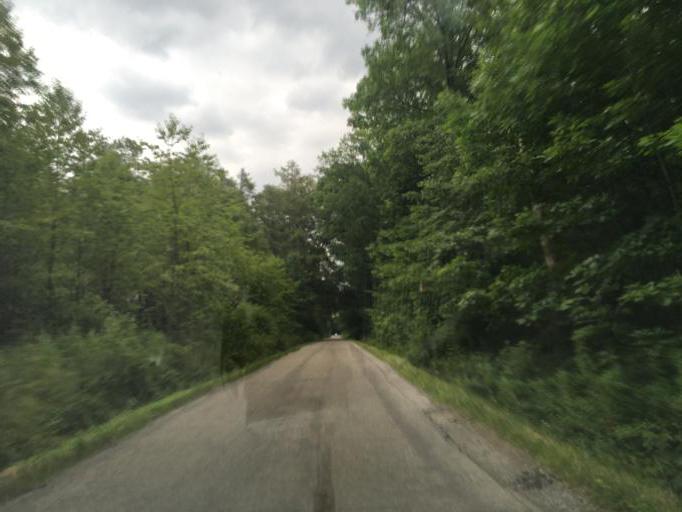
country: DE
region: Baden-Wuerttemberg
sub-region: Tuebingen Region
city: Kusterdingen
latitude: 48.5647
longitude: 9.1167
